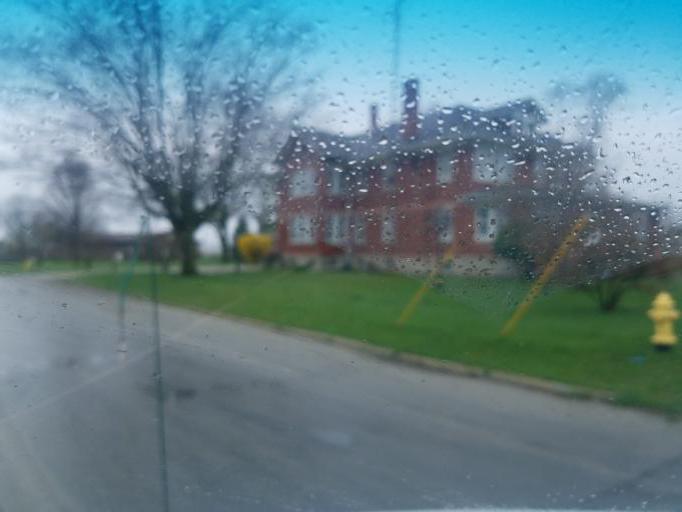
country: US
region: Ohio
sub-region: Wood County
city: North Baltimore
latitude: 41.2400
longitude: -83.6403
